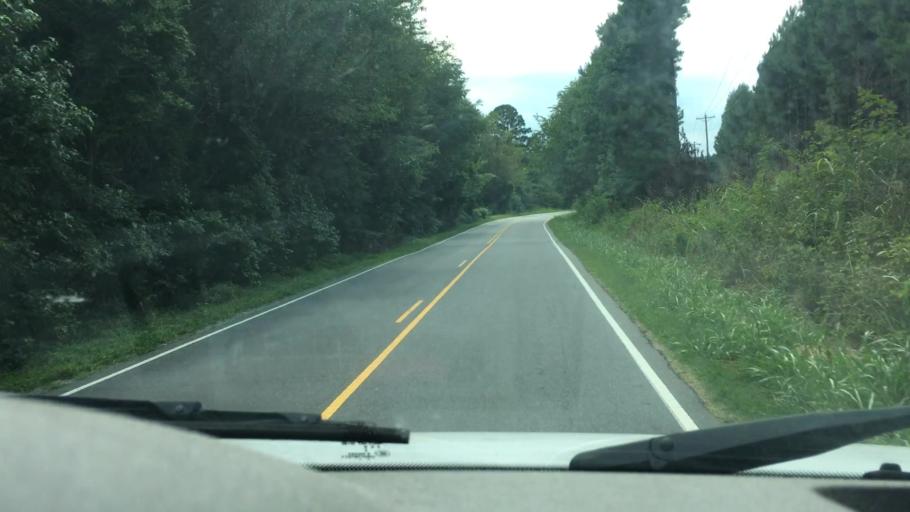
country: US
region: North Carolina
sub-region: Gaston County
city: Davidson
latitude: 35.4834
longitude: -80.8170
